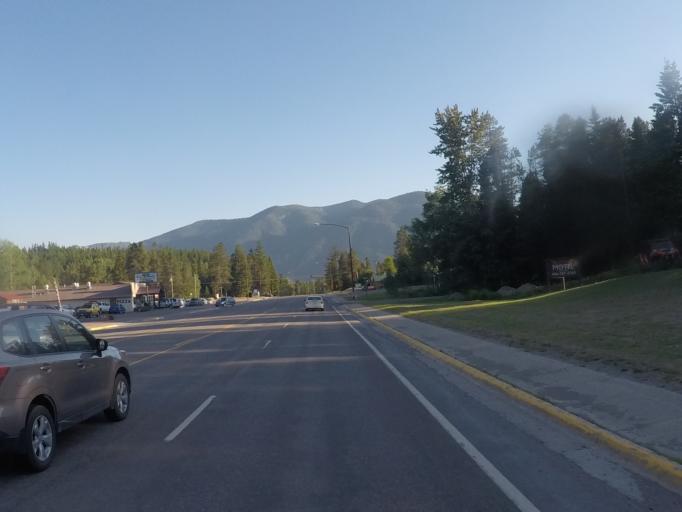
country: US
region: Montana
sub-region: Flathead County
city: Columbia Falls
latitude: 48.4199
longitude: -114.0461
